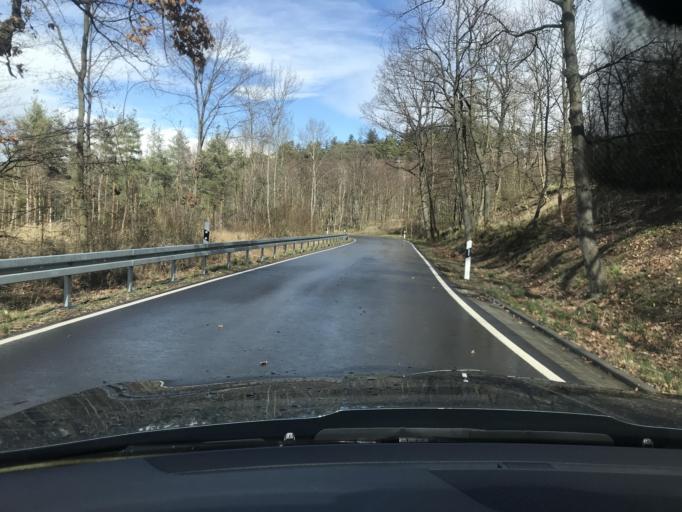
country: DE
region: Saxony-Anhalt
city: Hoym
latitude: 51.7095
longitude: 11.3129
